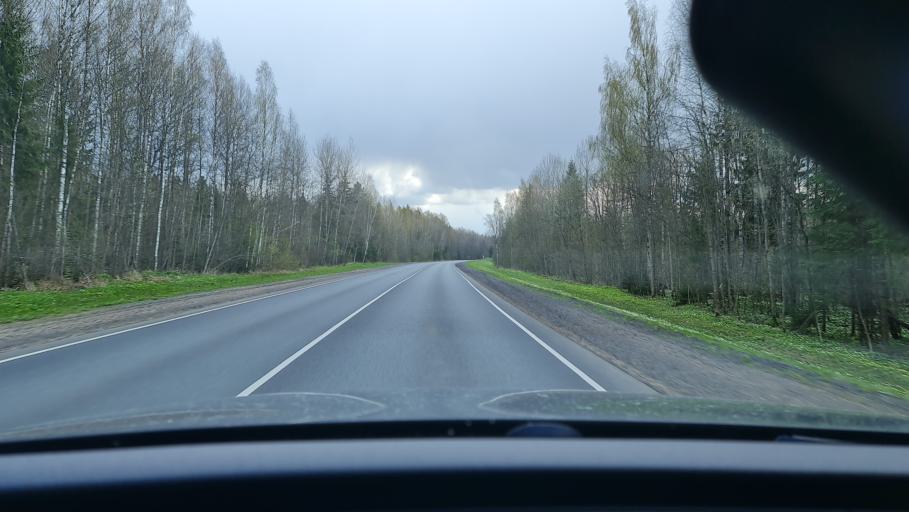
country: RU
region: Tverskaya
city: Nelidovo
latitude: 56.3061
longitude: 32.4629
